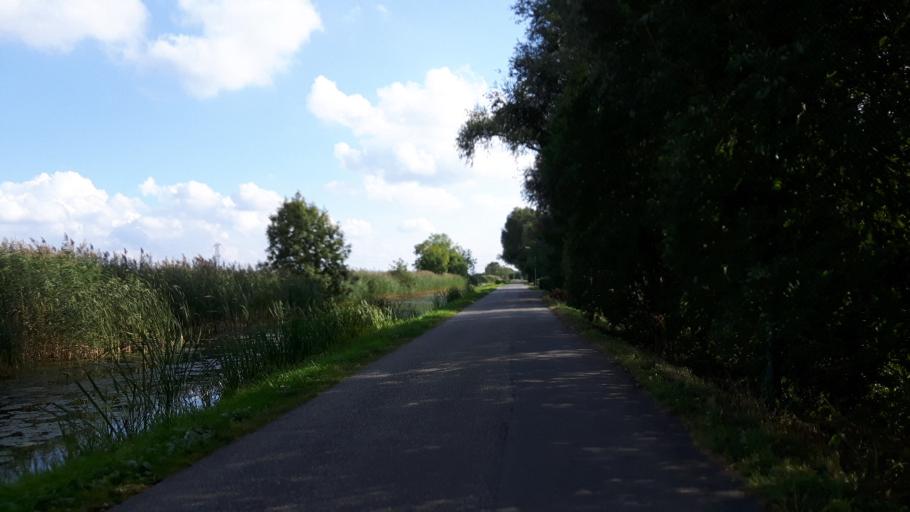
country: NL
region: Utrecht
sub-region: Stichtse Vecht
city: Breukelen
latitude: 52.1379
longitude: 4.9572
